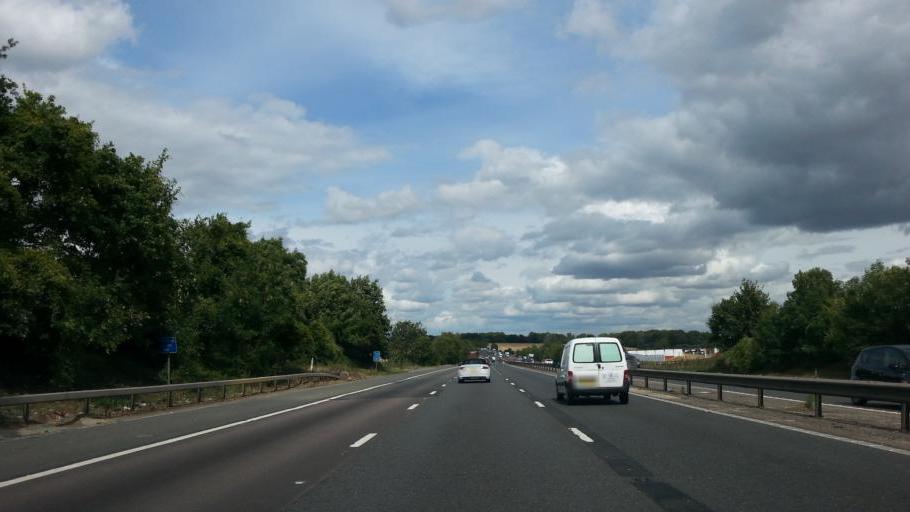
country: GB
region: England
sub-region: Hertfordshire
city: Sawbridgeworth
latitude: 51.7892
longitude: 0.1709
